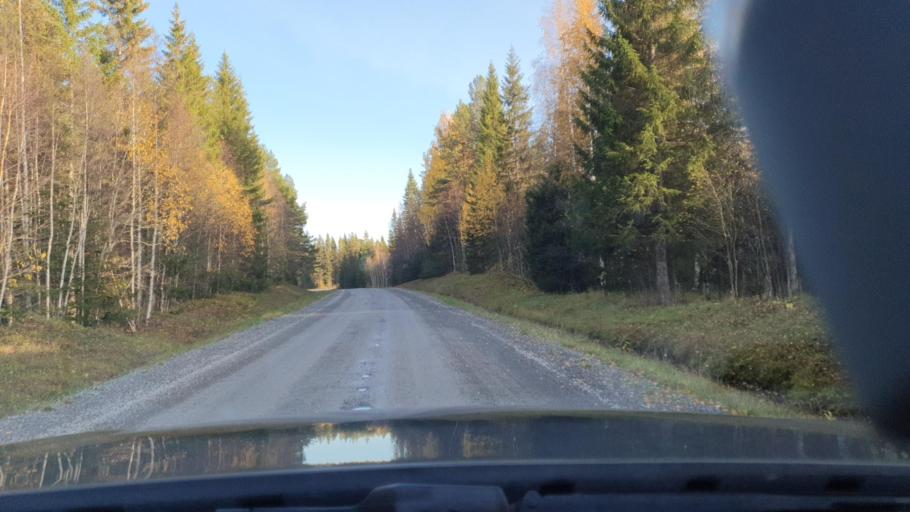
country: SE
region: Jaemtland
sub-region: Stroemsunds Kommun
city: Stroemsund
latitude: 63.5437
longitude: 15.5653
